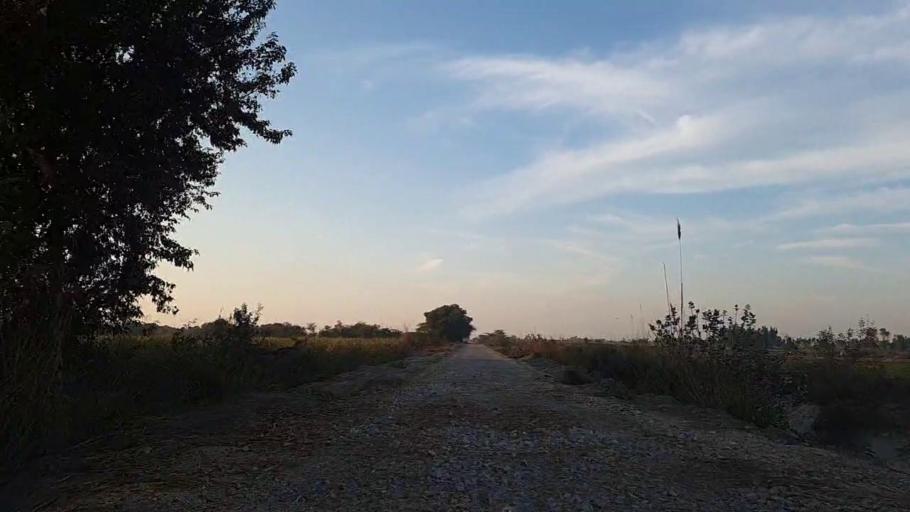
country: PK
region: Sindh
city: Bandhi
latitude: 26.6157
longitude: 68.3546
